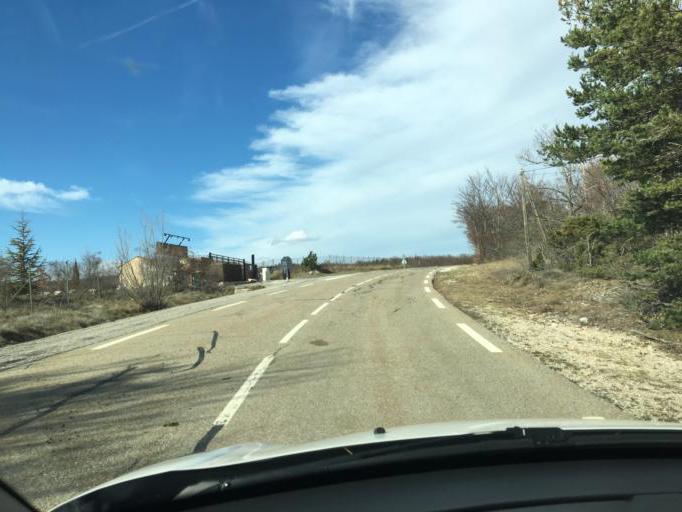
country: FR
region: Provence-Alpes-Cote d'Azur
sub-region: Departement du Vaucluse
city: Saint-Saturnin-les-Apt
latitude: 43.9747
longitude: 5.4664
